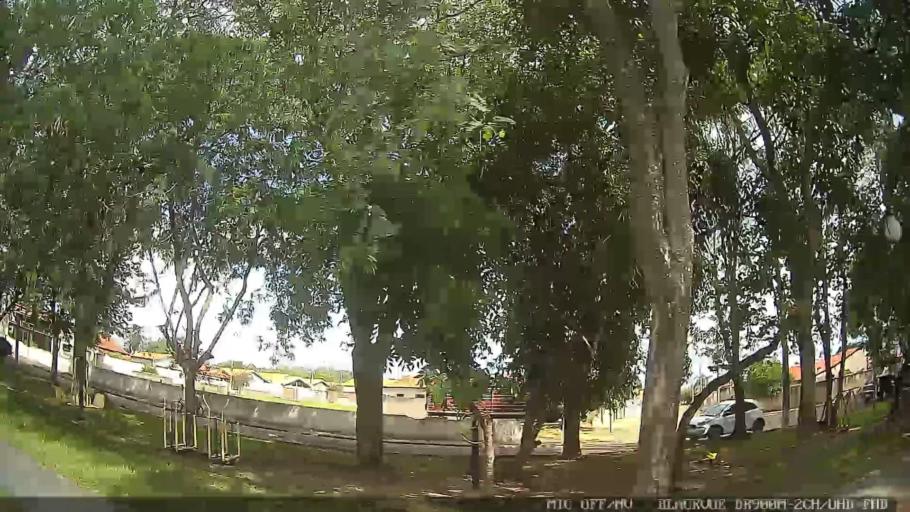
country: BR
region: Sao Paulo
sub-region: Conchas
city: Conchas
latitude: -23.0682
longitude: -47.9759
